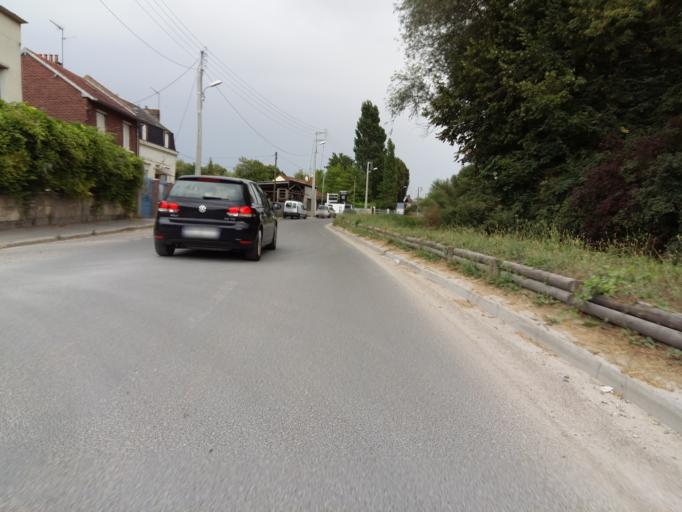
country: FR
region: Picardie
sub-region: Departement de la Somme
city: Rivery
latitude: 49.8909
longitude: 2.3248
